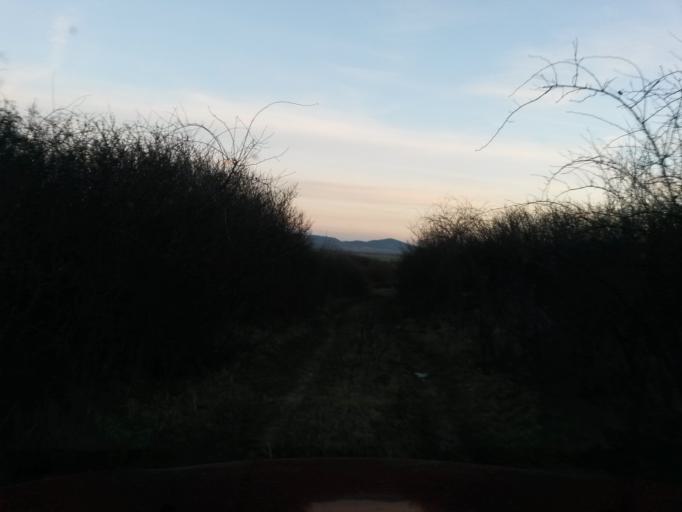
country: SK
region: Kosicky
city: Kosice
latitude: 48.7046
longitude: 21.3219
